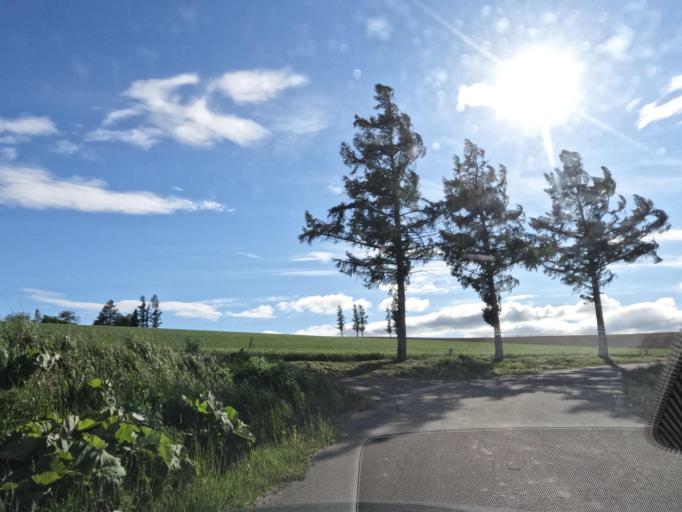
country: JP
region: Hokkaido
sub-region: Asahikawa-shi
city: Asahikawa
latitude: 43.5977
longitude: 142.4295
